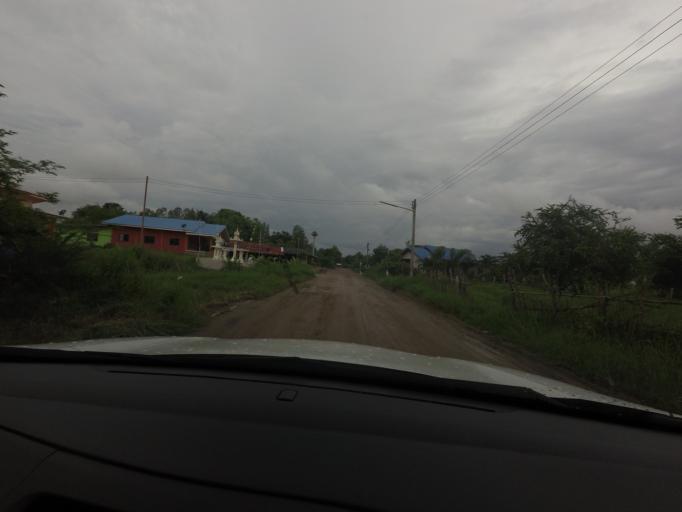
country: TH
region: Nakhon Ratchasima
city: Pak Chong
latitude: 14.6451
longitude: 101.4384
